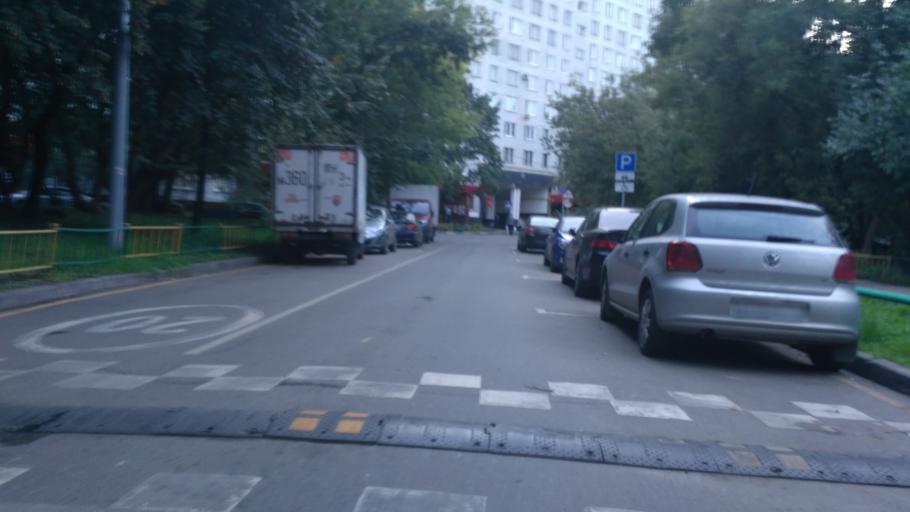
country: RU
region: Moscow
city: Ostankinskiy
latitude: 55.8189
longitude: 37.6279
